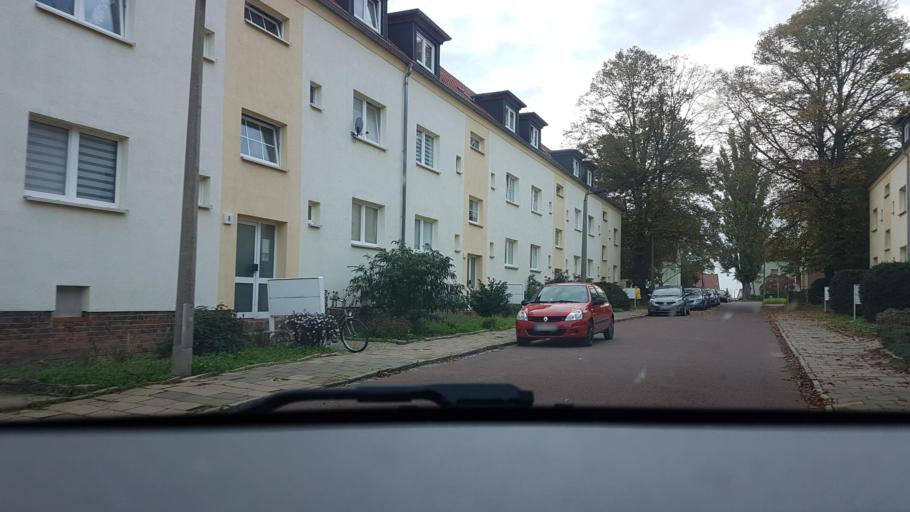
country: DE
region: Saxony-Anhalt
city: Bernburg
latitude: 51.7822
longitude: 11.7630
